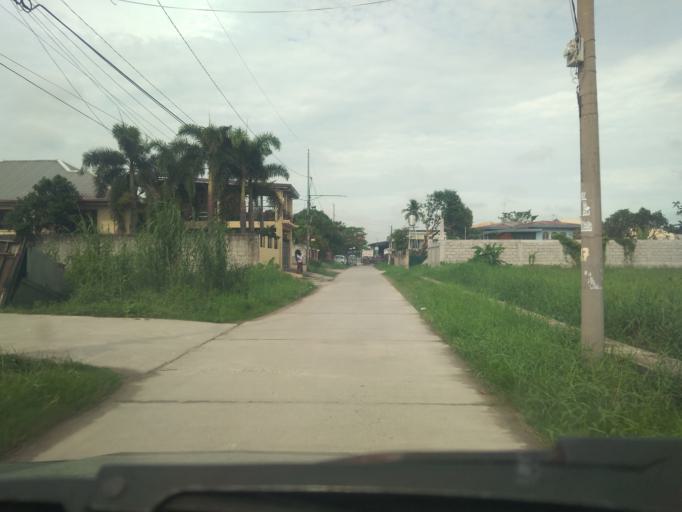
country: PH
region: Central Luzon
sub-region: Province of Pampanga
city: Pau
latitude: 15.0048
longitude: 120.7142
